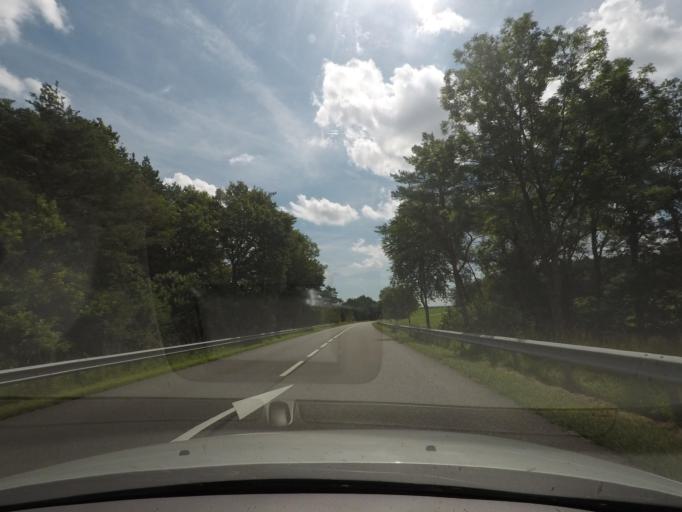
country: FR
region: Alsace
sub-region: Departement du Bas-Rhin
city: Drulingen
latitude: 48.8703
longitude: 7.1707
